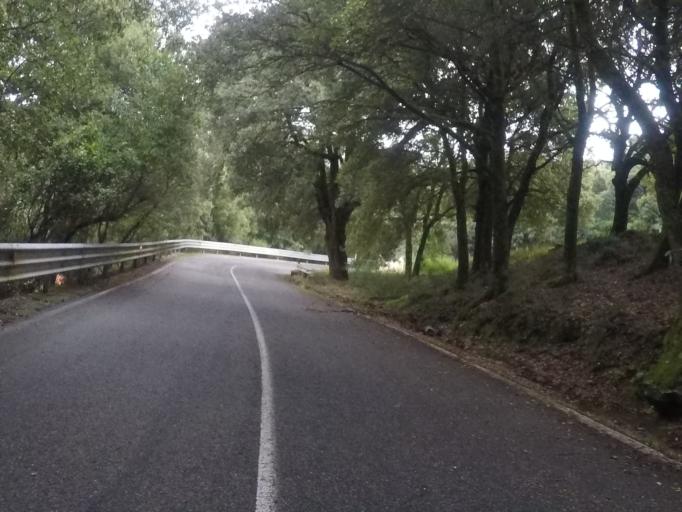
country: IT
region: Sardinia
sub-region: Provincia di Oristano
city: Cuglieri
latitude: 40.1707
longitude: 8.6071
